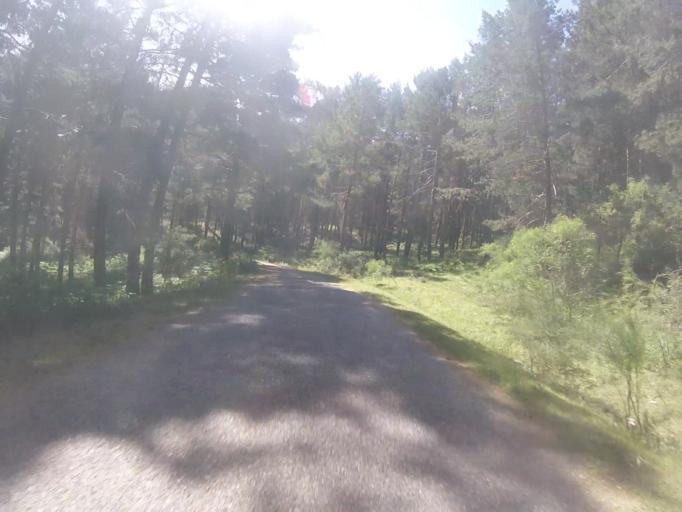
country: ES
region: Madrid
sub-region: Provincia de Madrid
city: Cercedilla
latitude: 40.8069
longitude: -4.0433
